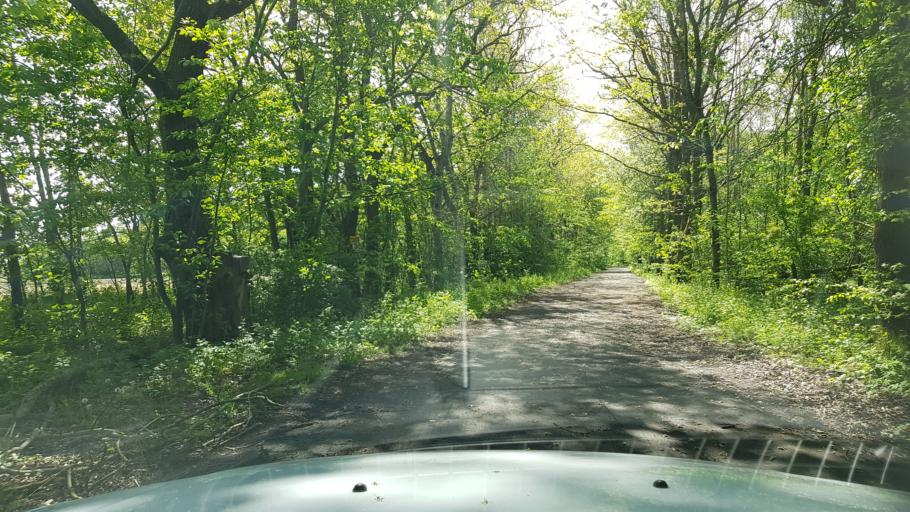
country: PL
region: West Pomeranian Voivodeship
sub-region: Powiat kolobrzeski
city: Ustronie Morskie
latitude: 54.2267
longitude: 15.8082
